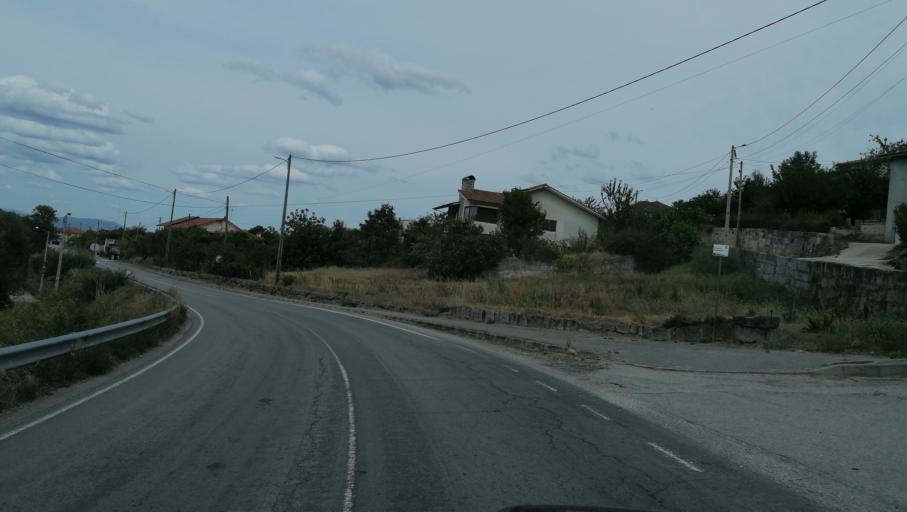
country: PT
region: Vila Real
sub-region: Vila Pouca de Aguiar
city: Vila Pouca de Aguiar
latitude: 41.5265
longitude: -7.6122
